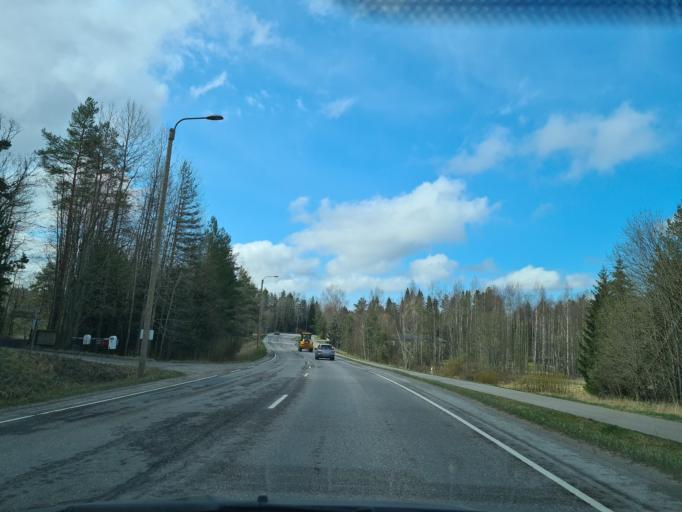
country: FI
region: Uusimaa
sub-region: Helsinki
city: Kirkkonummi
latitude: 60.0990
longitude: 24.4170
